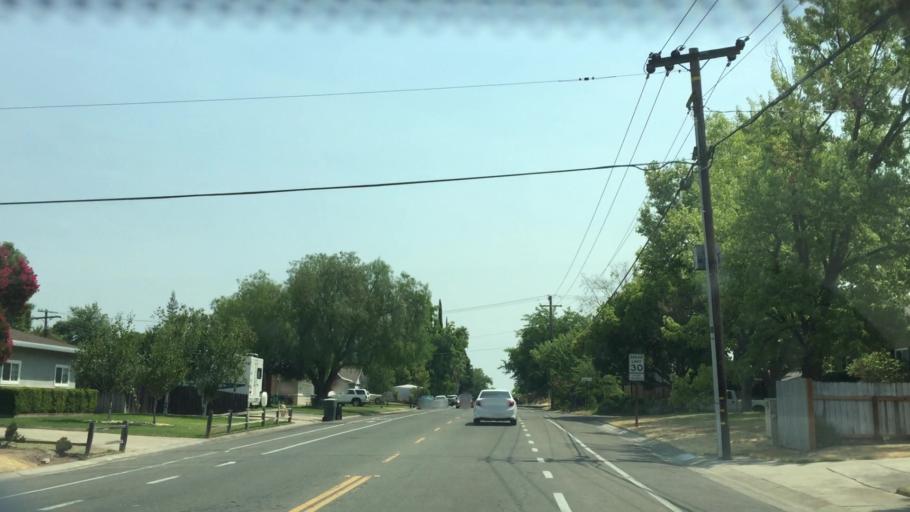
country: US
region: California
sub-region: Sacramento County
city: Arden-Arcade
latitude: 38.6030
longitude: -121.3642
